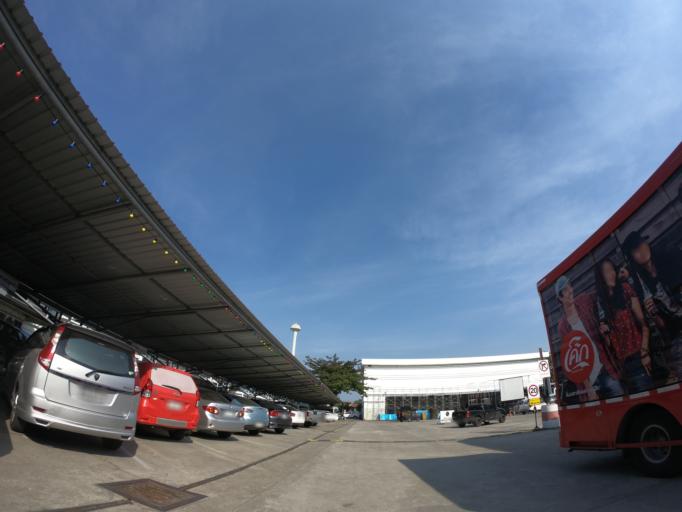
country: TH
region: Chiang Mai
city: Chiang Mai
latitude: 18.8191
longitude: 98.9824
